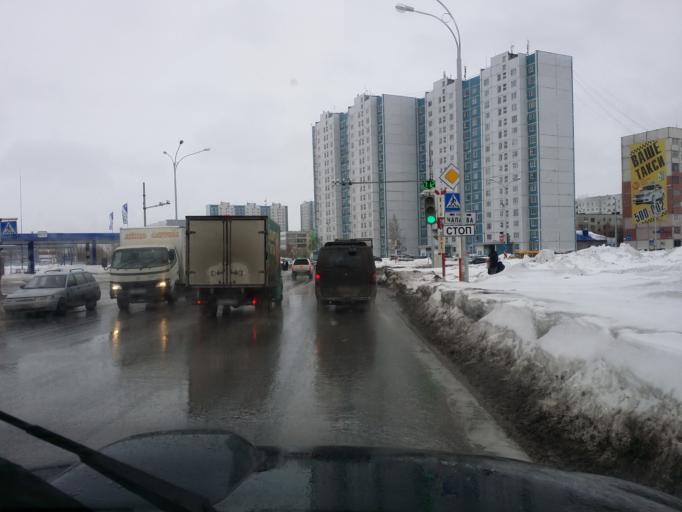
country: RU
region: Khanty-Mansiyskiy Avtonomnyy Okrug
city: Nizhnevartovsk
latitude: 60.9518
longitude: 76.6076
